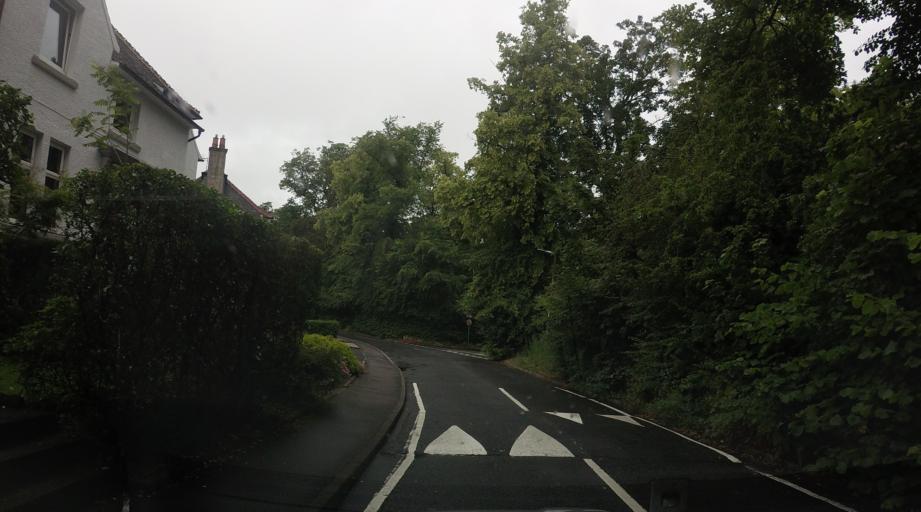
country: GB
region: Scotland
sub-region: West Lothian
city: Broxburn
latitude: 55.9294
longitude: -3.5007
